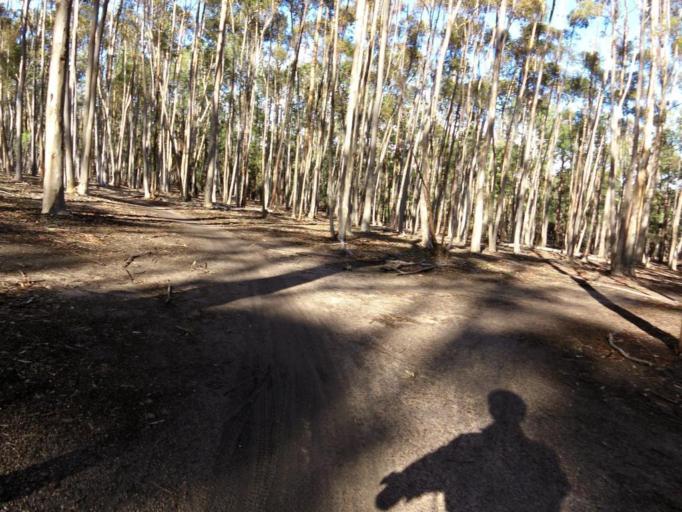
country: AU
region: Victoria
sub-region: Greater Geelong
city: Lara
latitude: -37.9542
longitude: 144.4049
